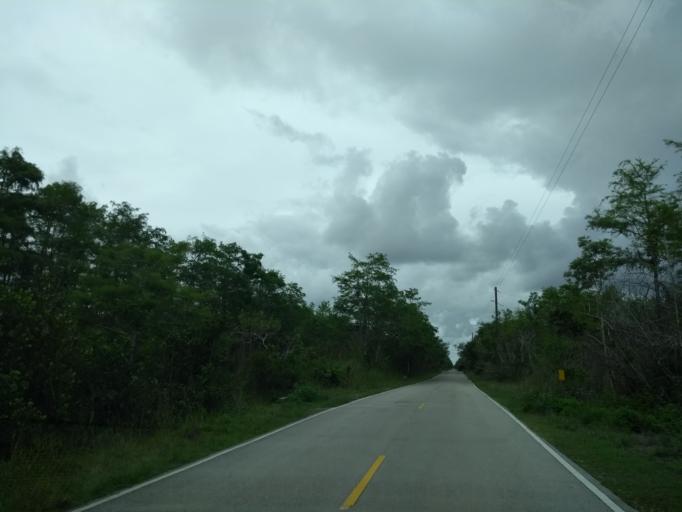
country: US
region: Florida
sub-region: Miami-Dade County
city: The Hammocks
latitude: 25.7613
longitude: -80.8994
